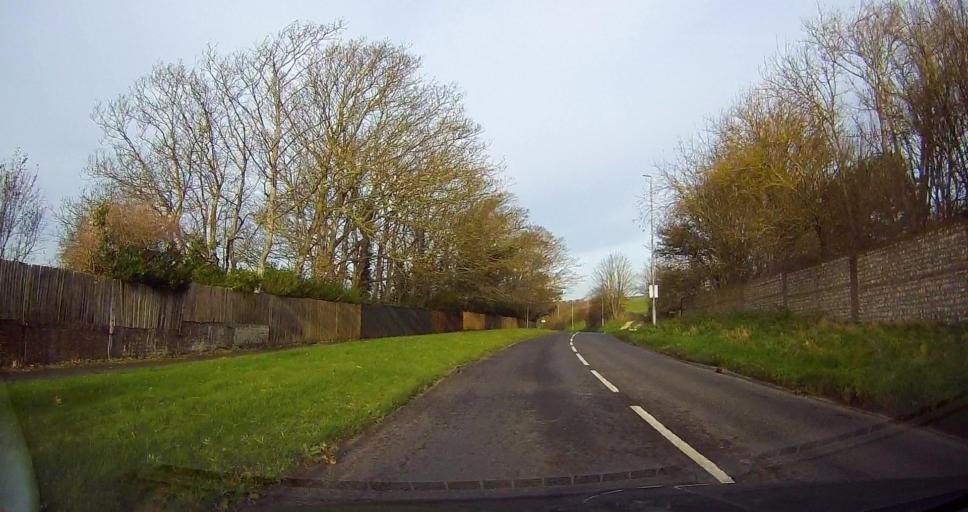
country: GB
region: England
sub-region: Brighton and Hove
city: Rottingdean
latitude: 50.8171
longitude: -0.0645
